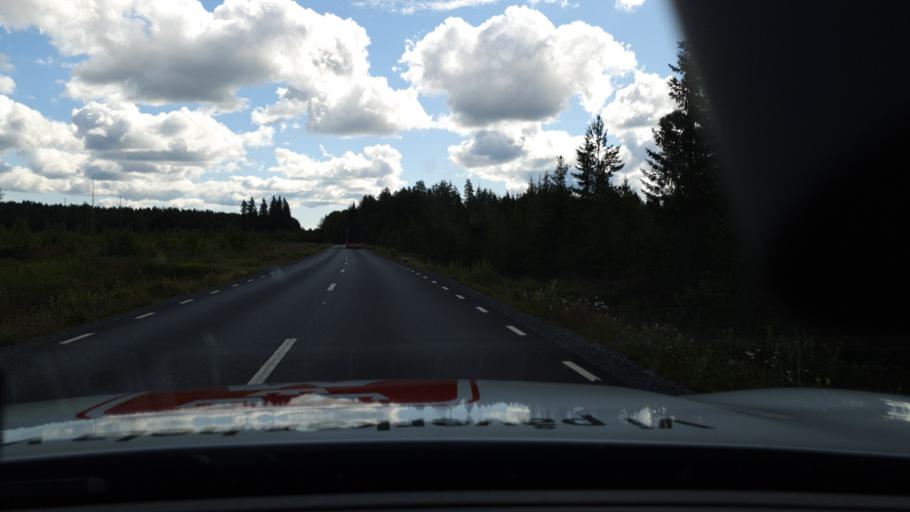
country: SE
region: Norrbotten
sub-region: Bodens Kommun
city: Saevast
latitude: 65.8399
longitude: 21.8162
